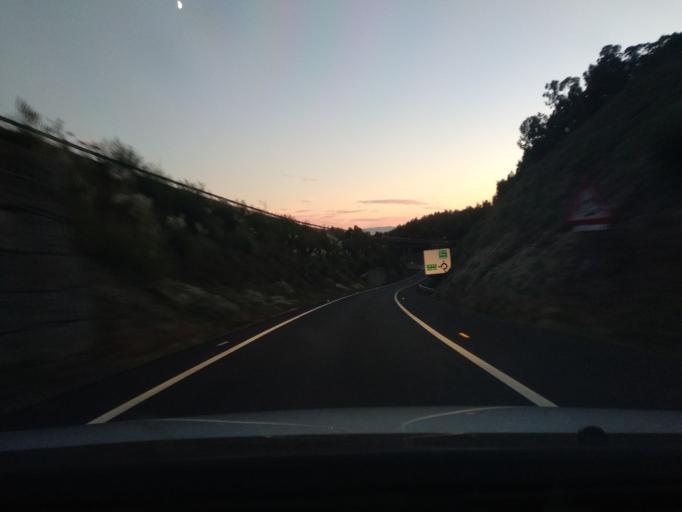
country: ES
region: Galicia
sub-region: Provincia de Pontevedra
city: Moana
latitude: 42.2865
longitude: -8.7542
